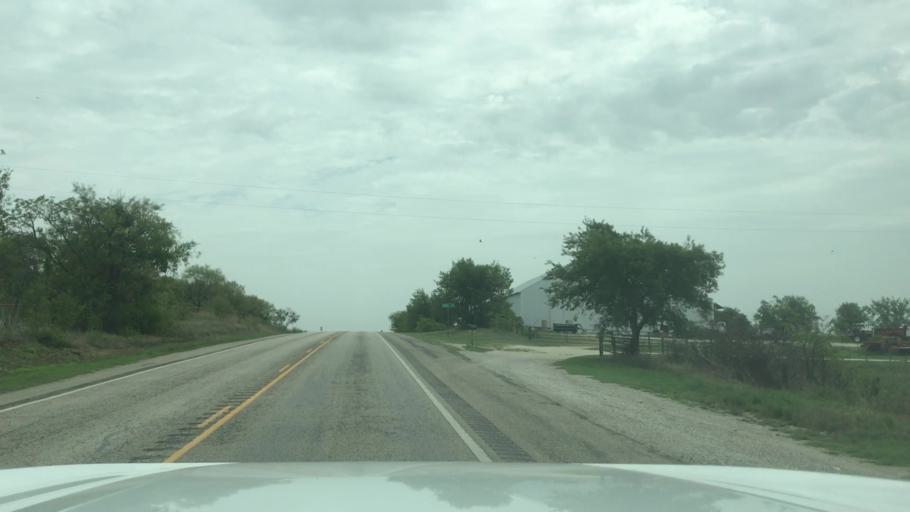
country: US
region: Texas
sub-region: Erath County
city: Dublin
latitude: 32.0584
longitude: -98.2036
